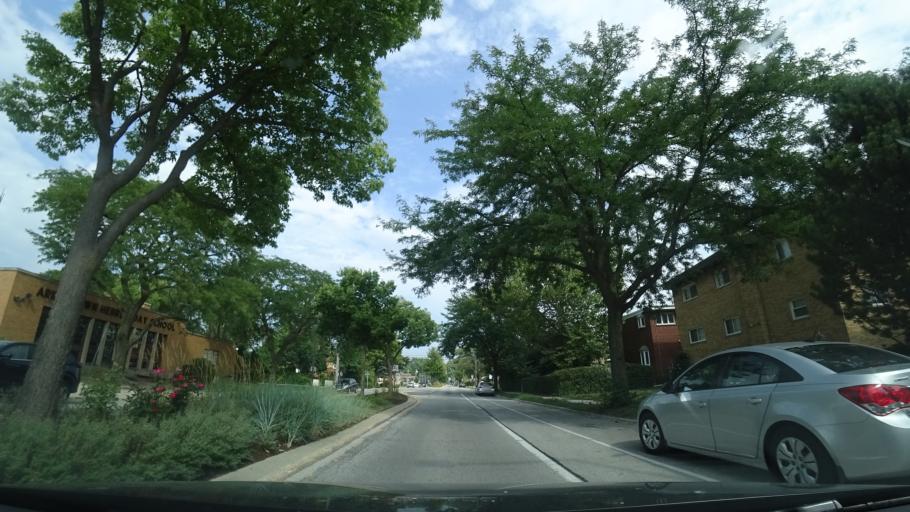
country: US
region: Illinois
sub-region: Cook County
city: Skokie
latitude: 42.0335
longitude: -87.7433
